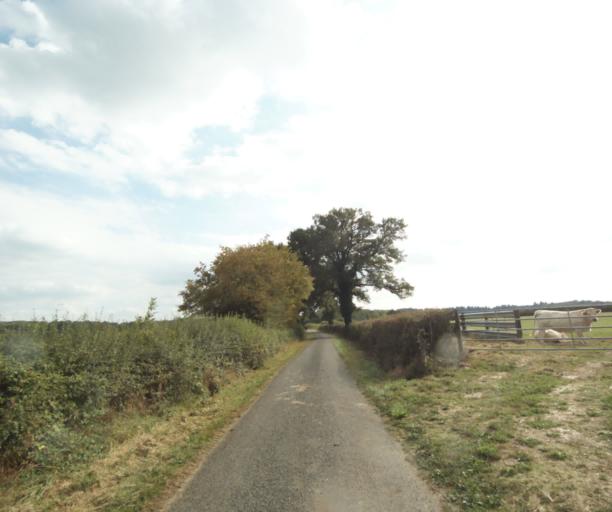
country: FR
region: Bourgogne
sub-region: Departement de Saone-et-Loire
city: Palinges
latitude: 46.5183
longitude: 4.2462
